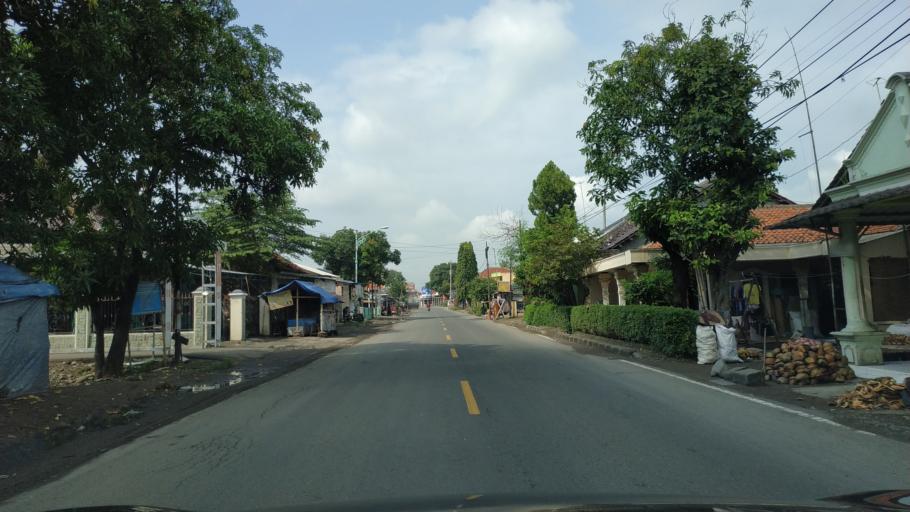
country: ID
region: Central Java
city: Ketanggungan
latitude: -6.8901
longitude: 108.8854
